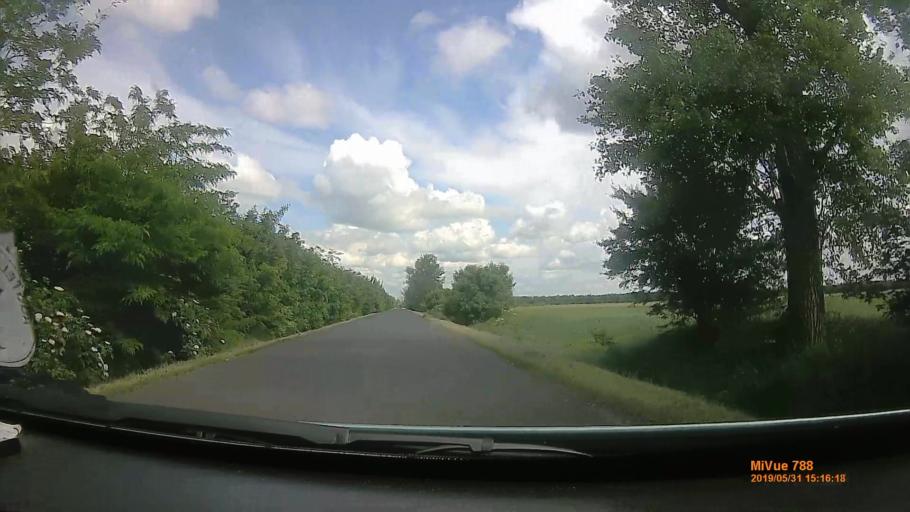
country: HU
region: Borsod-Abauj-Zemplen
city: Taktaharkany
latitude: 48.0885
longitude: 21.0963
